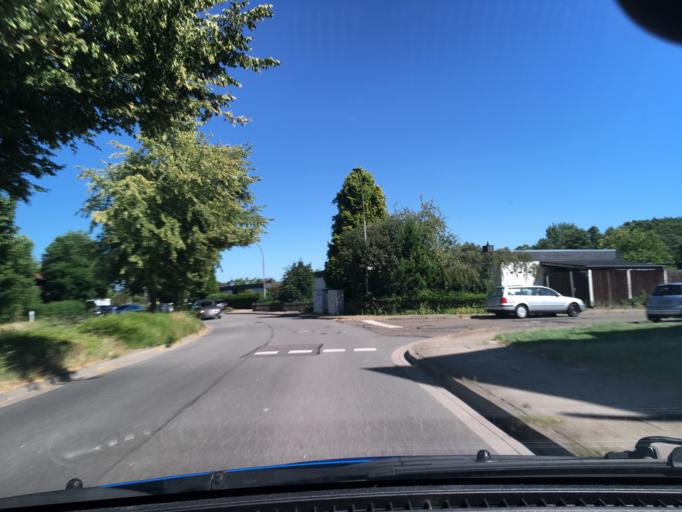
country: DE
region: Lower Saxony
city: Seevetal
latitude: 53.3844
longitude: 9.9917
